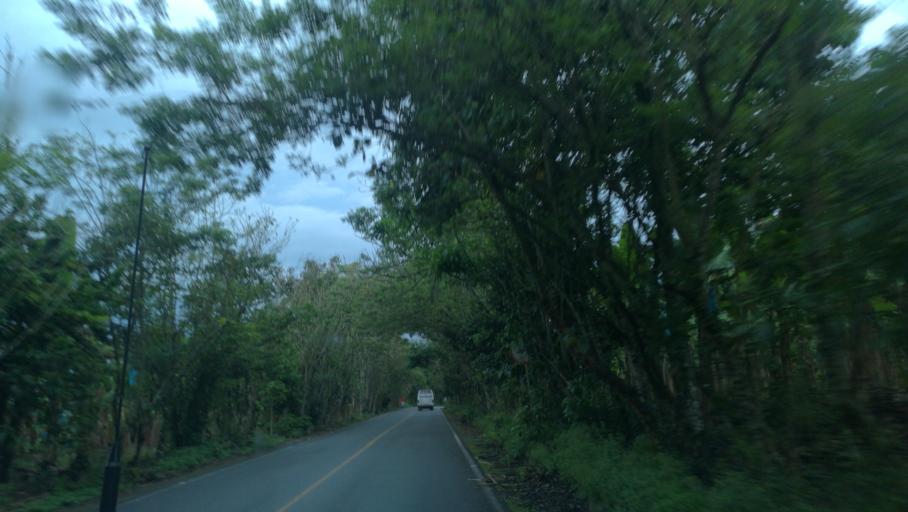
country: CO
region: Quindio
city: La Tebaida
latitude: 4.5090
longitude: -75.7687
